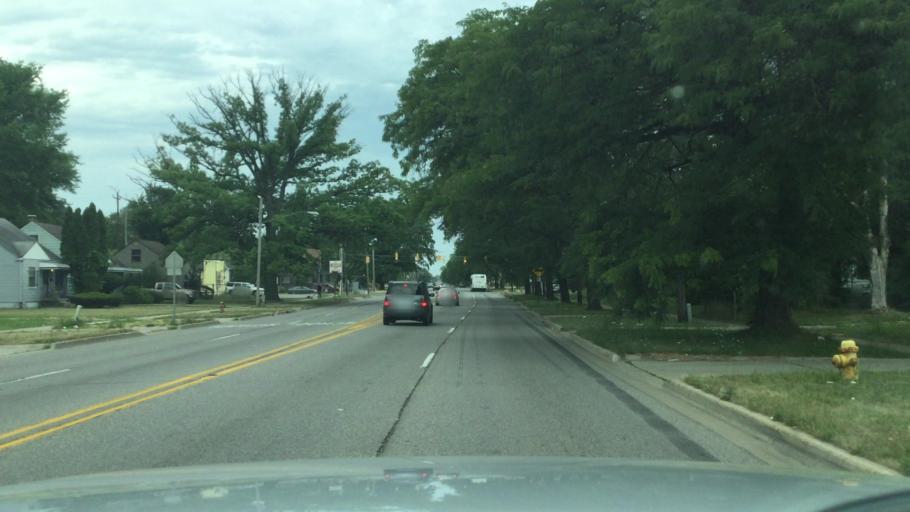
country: US
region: Michigan
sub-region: Genesee County
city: Beecher
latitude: 43.0610
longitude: -83.7121
